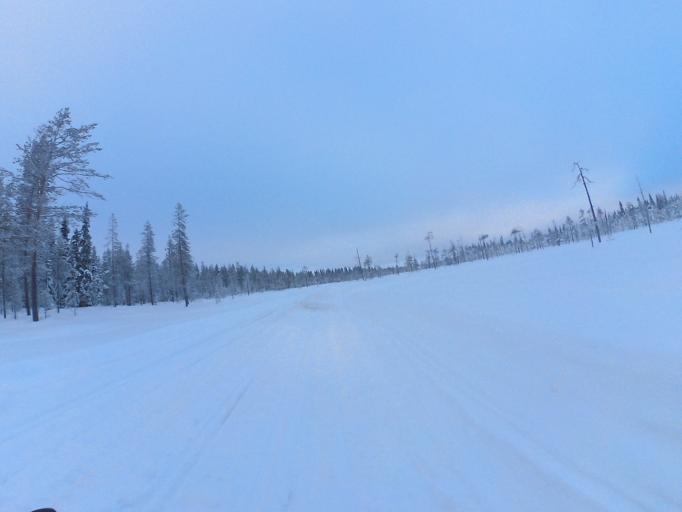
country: FI
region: Lapland
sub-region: Rovaniemi
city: Rovaniemi
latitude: 66.6352
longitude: 26.0393
